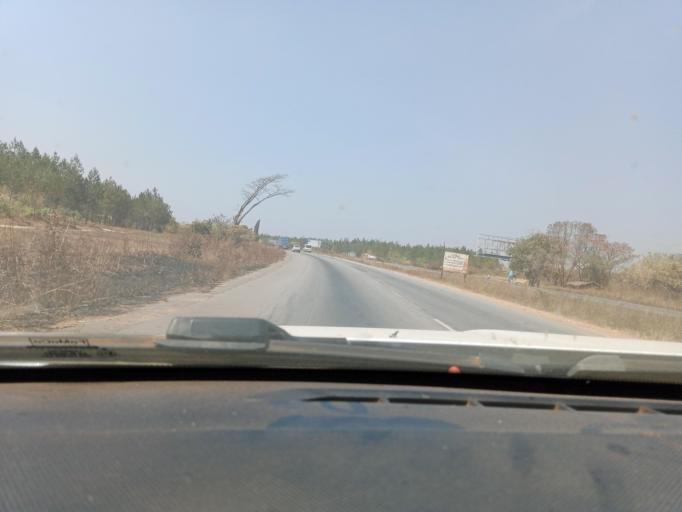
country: ZM
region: Copperbelt
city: Luanshya
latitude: -13.0408
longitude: 28.4595
